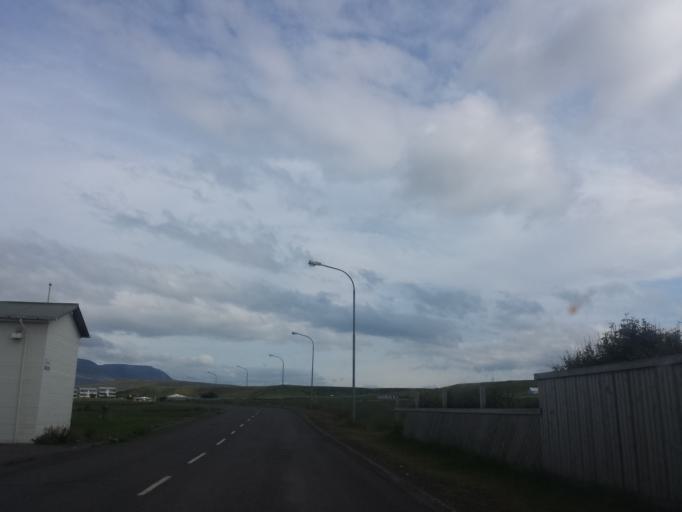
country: IS
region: Northwest
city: Saudarkrokur
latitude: 65.6595
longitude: -20.2999
